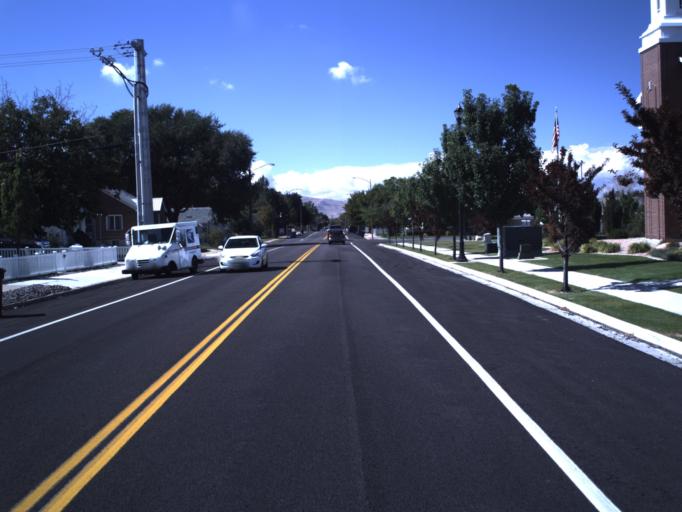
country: US
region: Utah
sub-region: Utah County
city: Spanish Fork
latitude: 40.1150
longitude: -111.6481
